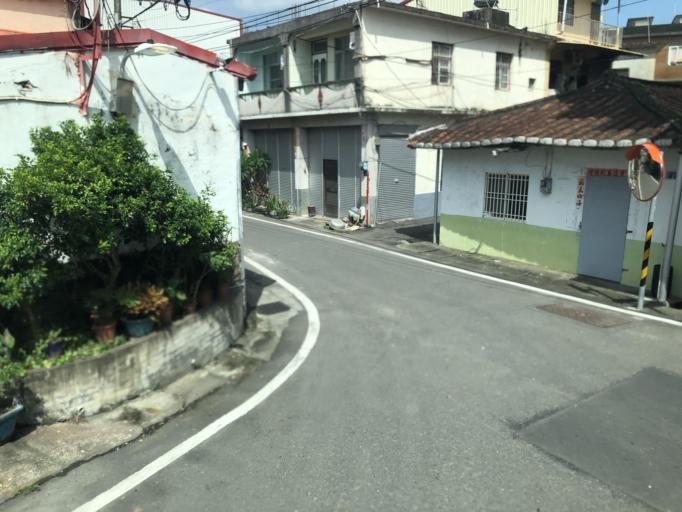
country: TW
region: Taiwan
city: Yujing
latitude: 22.9149
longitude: 120.5655
